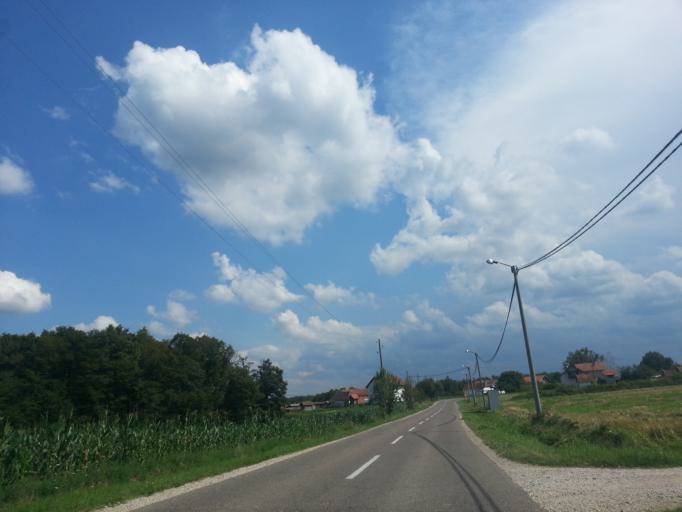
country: HR
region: Vukovarsko-Srijemska
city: Gunja
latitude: 44.8192
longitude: 18.8412
